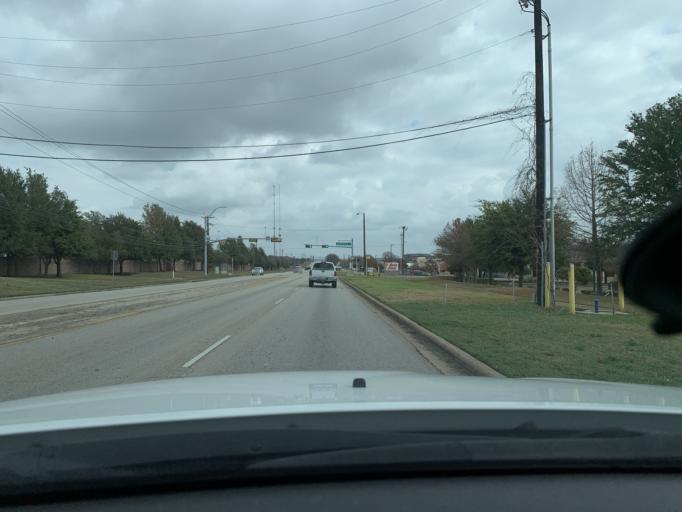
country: US
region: Texas
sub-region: Williamson County
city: Round Rock
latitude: 30.5669
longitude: -97.6657
